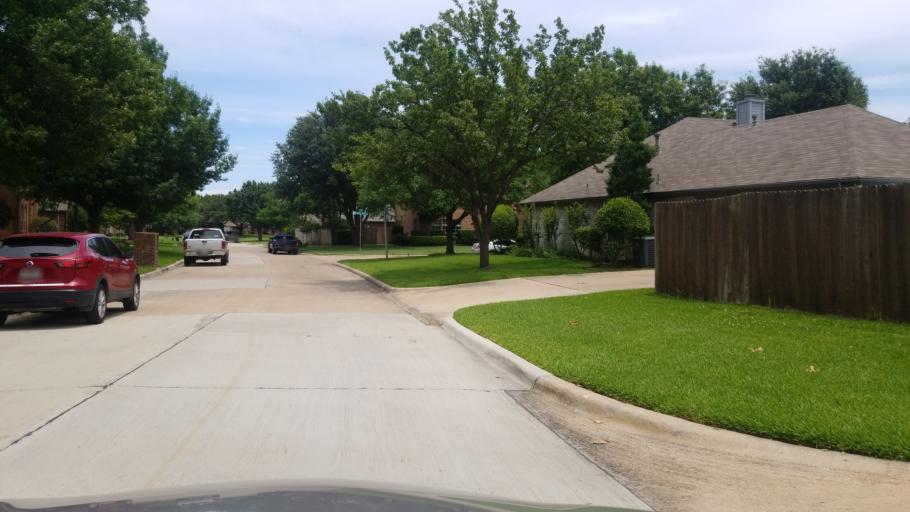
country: US
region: Texas
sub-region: Dallas County
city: Grand Prairie
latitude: 32.6801
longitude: -96.9884
